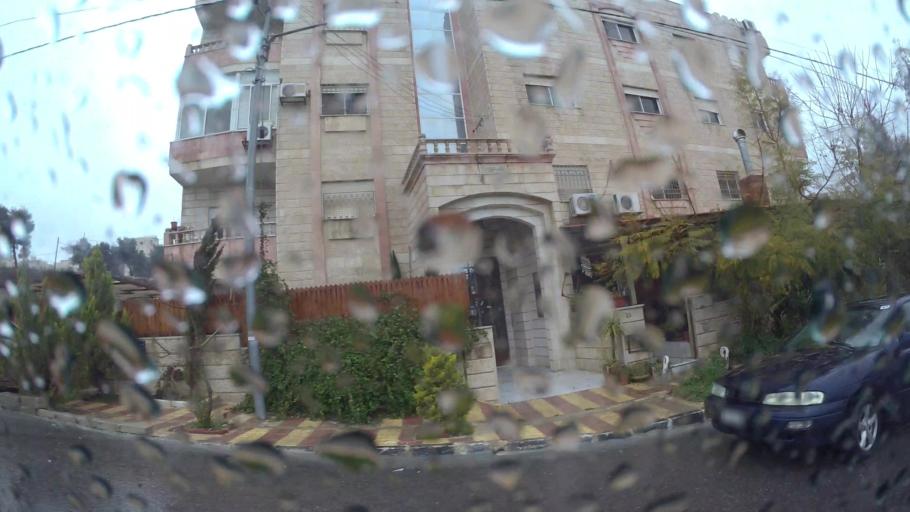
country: JO
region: Amman
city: Al Jubayhah
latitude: 32.0312
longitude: 35.8875
